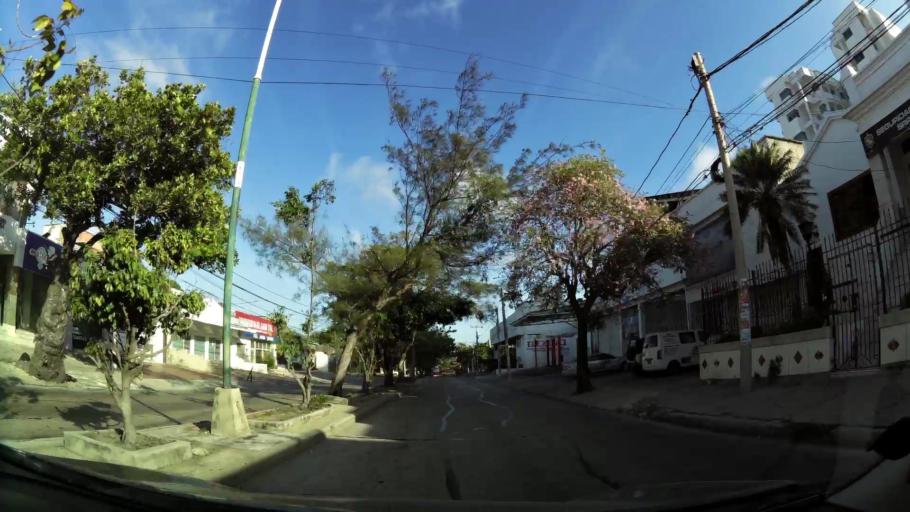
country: CO
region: Atlantico
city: Barranquilla
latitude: 10.9984
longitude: -74.8129
